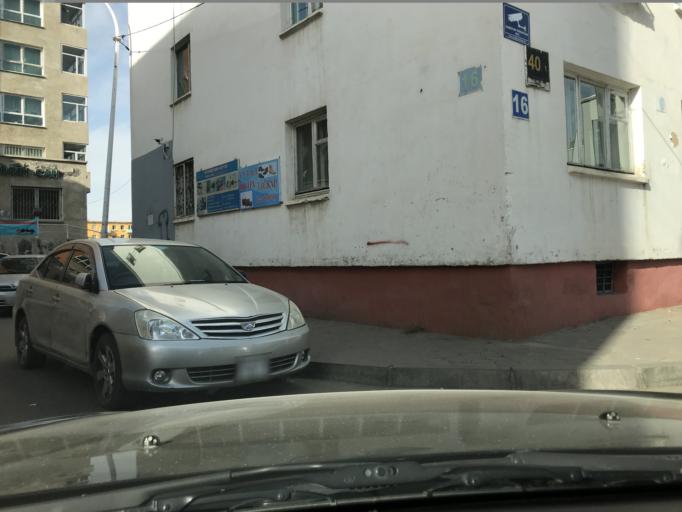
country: MN
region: Ulaanbaatar
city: Ulaanbaatar
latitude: 47.9184
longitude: 106.9031
